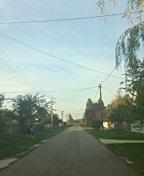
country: HU
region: Fejer
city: Ivancsa
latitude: 47.1795
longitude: 18.8668
